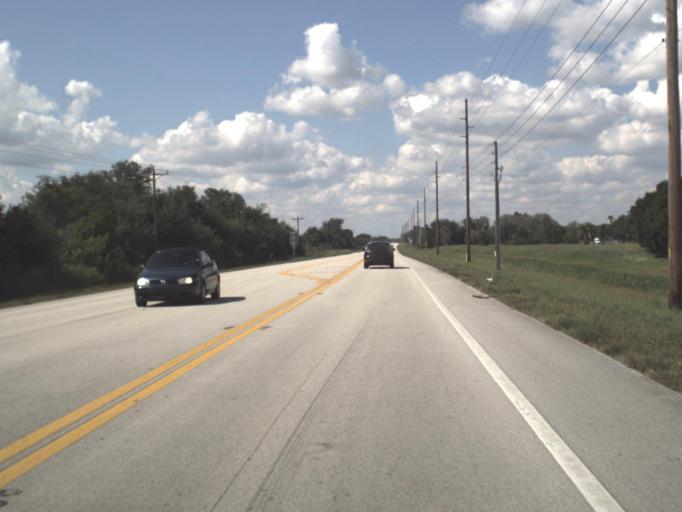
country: US
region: Florida
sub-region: Highlands County
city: Sebring
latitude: 27.4339
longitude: -81.3353
